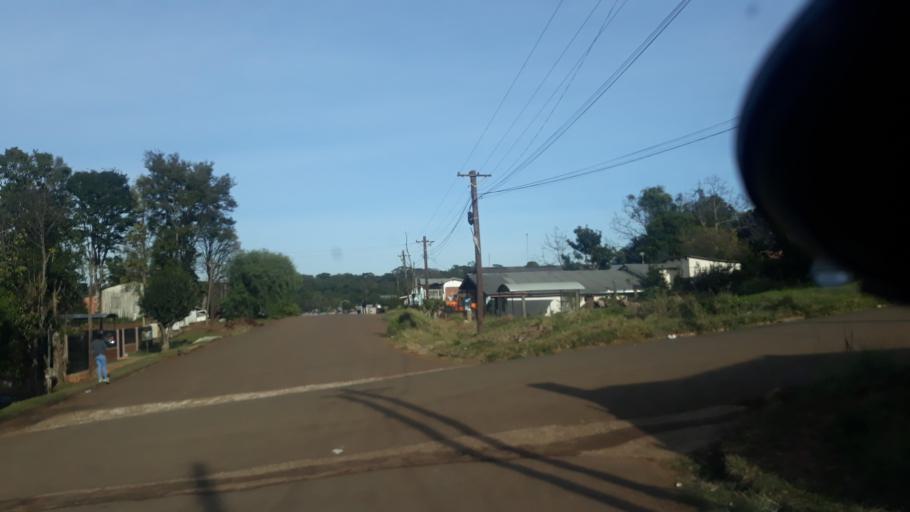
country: AR
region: Misiones
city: Bernardo de Irigoyen
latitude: -26.2648
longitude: -53.6510
